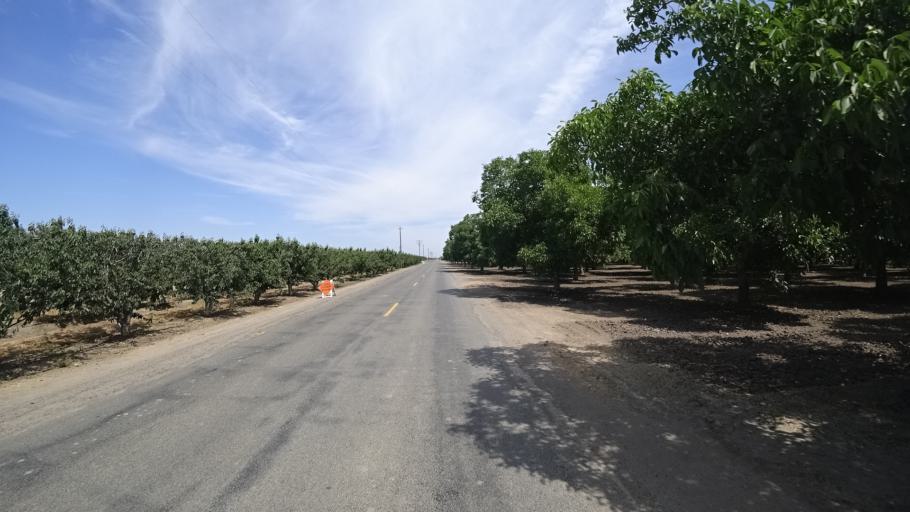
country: US
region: California
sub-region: Kings County
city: Lucerne
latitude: 36.3662
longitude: -119.6909
